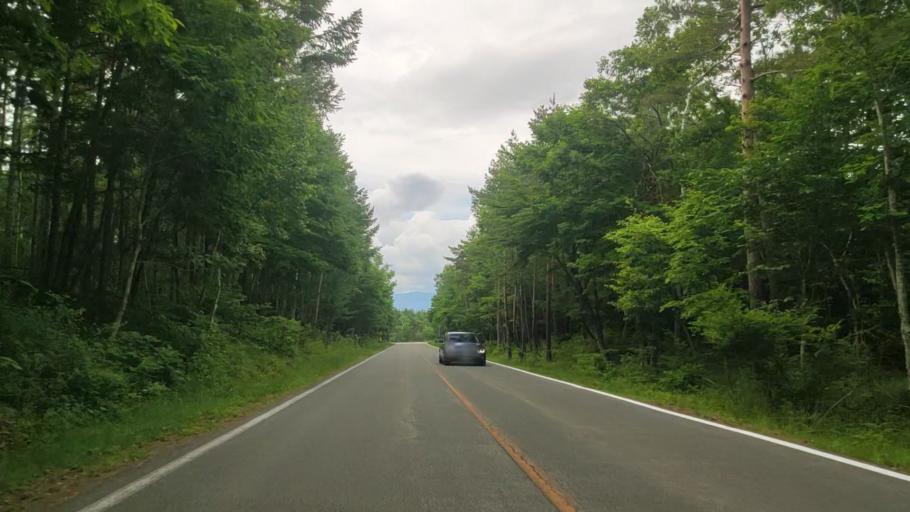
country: JP
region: Yamanashi
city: Fujikawaguchiko
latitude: 35.4283
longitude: 138.7393
